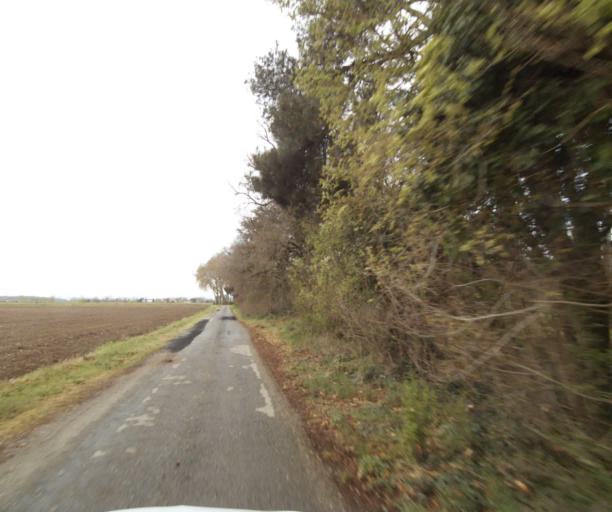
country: FR
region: Midi-Pyrenees
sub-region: Departement de l'Ariege
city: Mazeres
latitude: 43.2341
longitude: 1.6276
